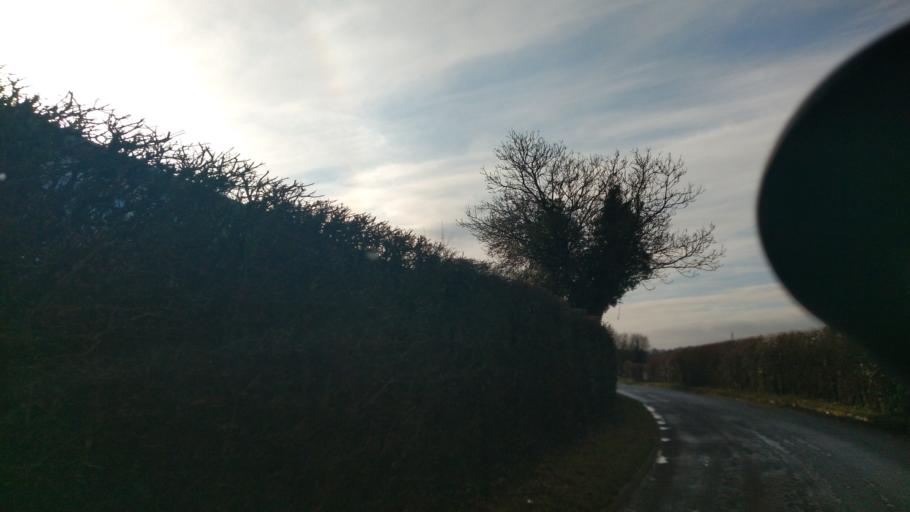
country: GB
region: England
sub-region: Wiltshire
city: Corsham
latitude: 51.4618
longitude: -2.1614
